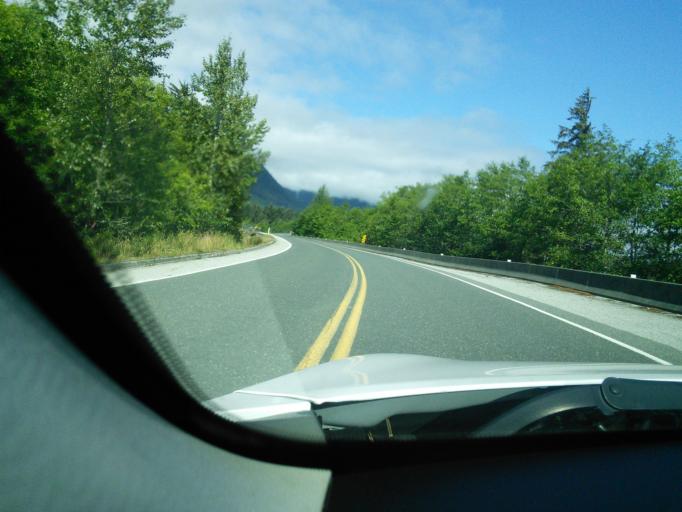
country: CA
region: British Columbia
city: Campbell River
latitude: 50.3606
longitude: -125.9150
